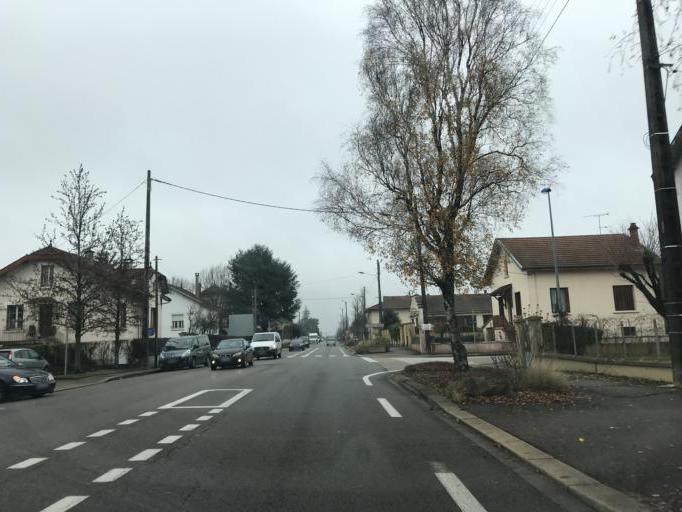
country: FR
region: Rhone-Alpes
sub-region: Departement de l'Ain
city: Peronnas
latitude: 46.2017
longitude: 5.2081
